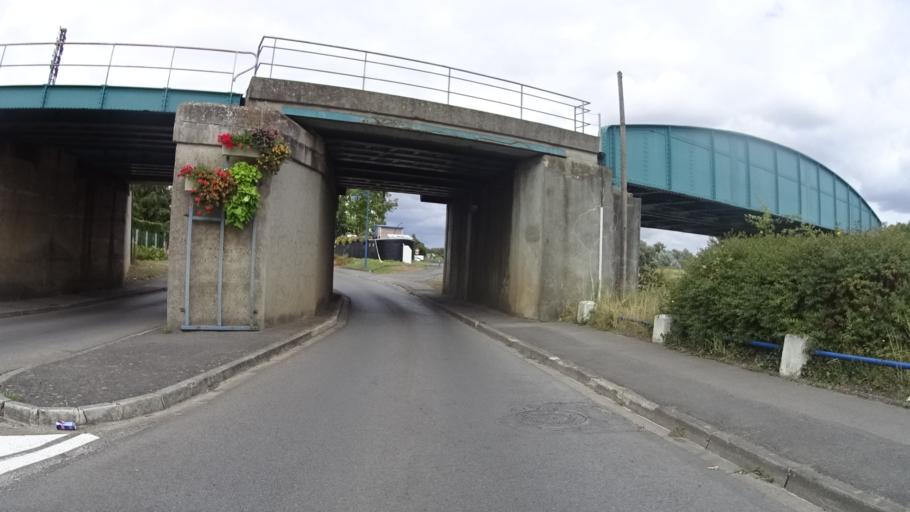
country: FR
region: Picardie
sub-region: Departement de l'Aisne
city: Beautor
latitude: 49.6568
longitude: 3.3471
